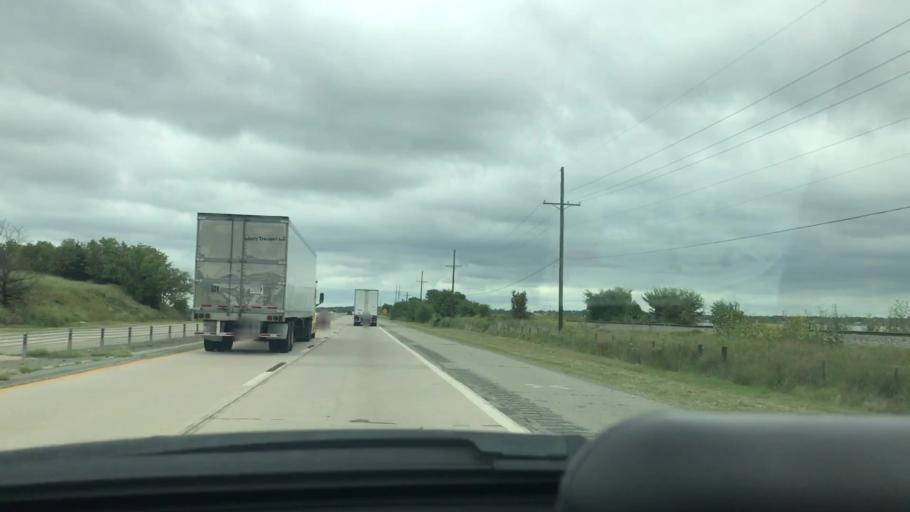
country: US
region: Oklahoma
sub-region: McIntosh County
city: Eufaula
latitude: 35.3268
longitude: -95.5876
